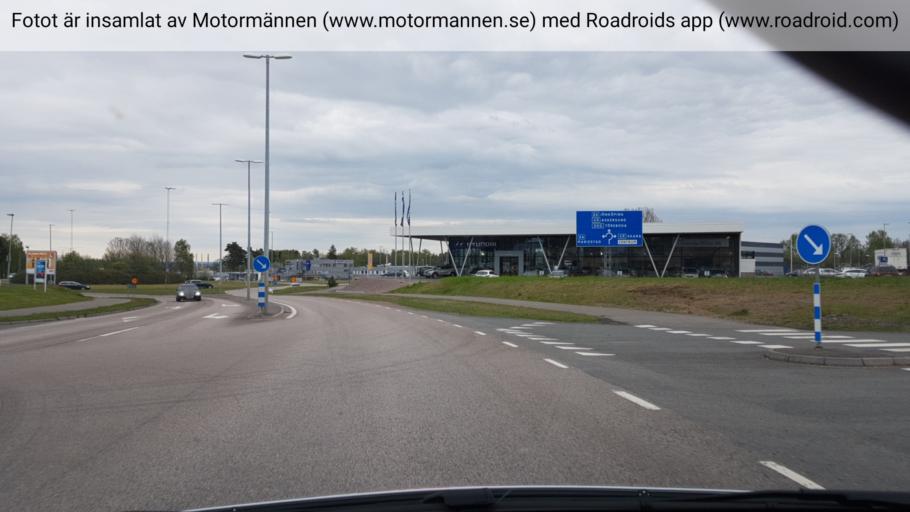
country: SE
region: Vaestra Goetaland
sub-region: Skovde Kommun
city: Skoevde
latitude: 58.4199
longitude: 13.8653
